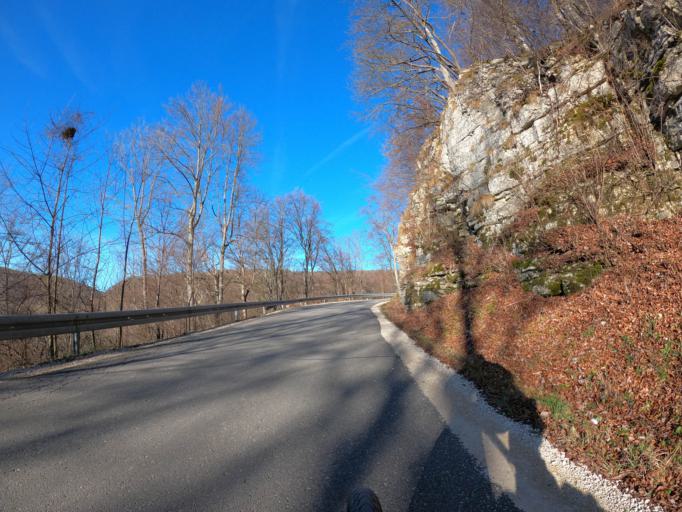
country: DE
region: Baden-Wuerttemberg
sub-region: Tuebingen Region
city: Sankt Johann
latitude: 48.4457
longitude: 9.2954
